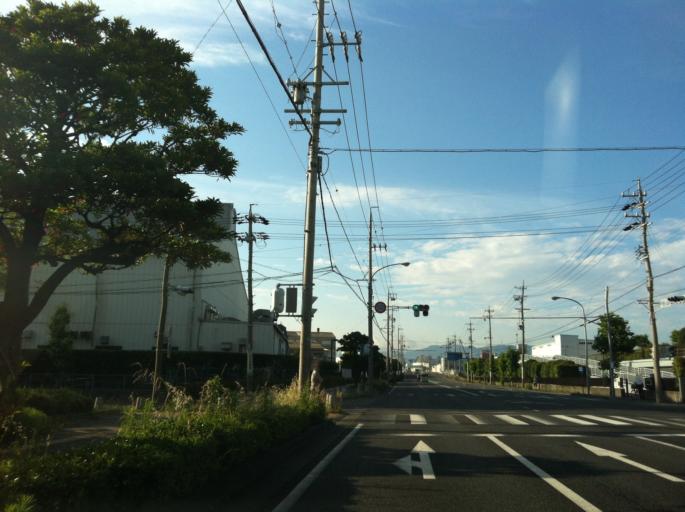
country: JP
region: Shizuoka
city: Shizuoka-shi
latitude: 34.9964
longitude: 138.4950
